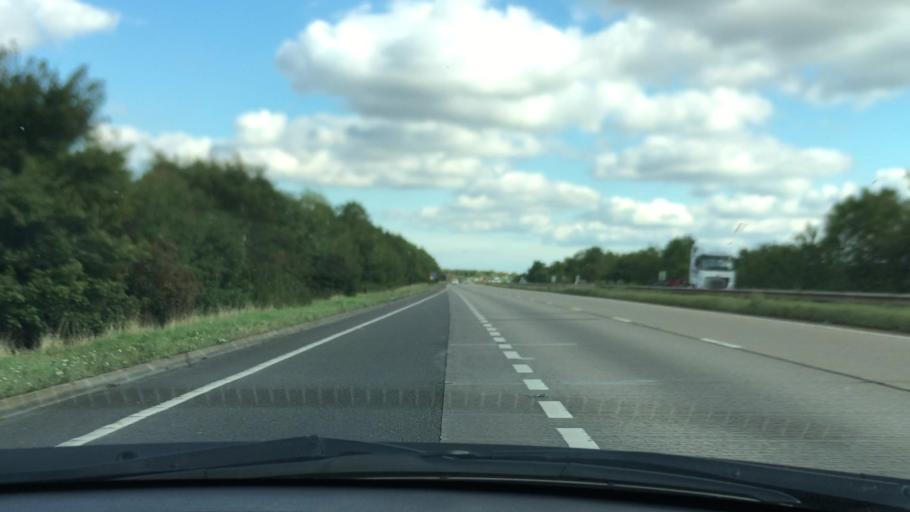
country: GB
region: England
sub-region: North East Lincolnshire
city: Healing
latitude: 53.5966
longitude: -0.1889
